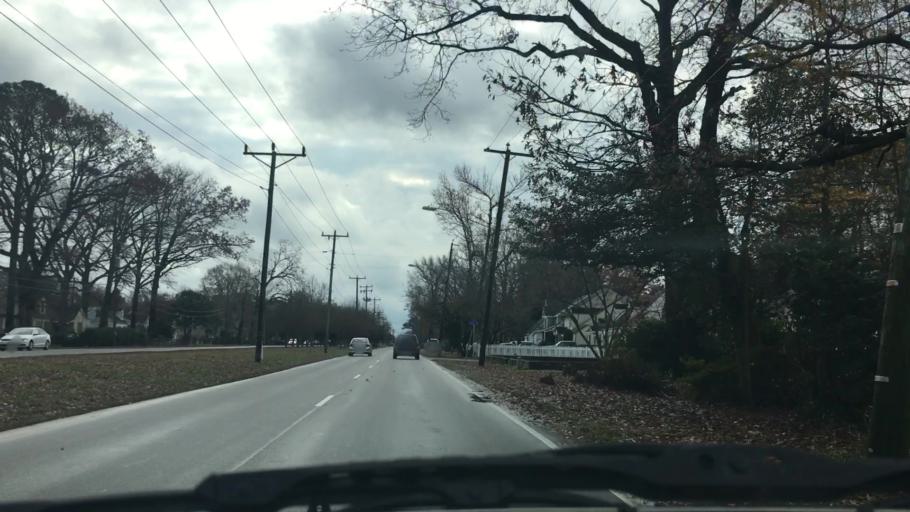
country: US
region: Virginia
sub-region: City of Norfolk
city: Norfolk
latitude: 36.9232
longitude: -76.2429
